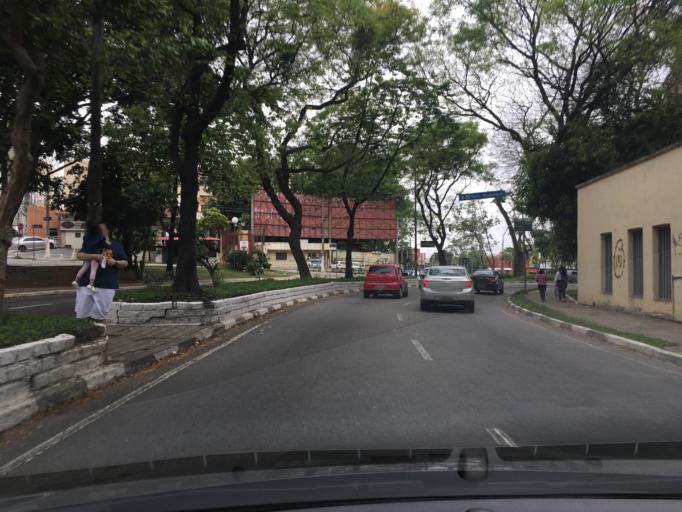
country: BR
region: Sao Paulo
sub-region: Guarulhos
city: Guarulhos
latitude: -23.4729
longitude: -46.5301
